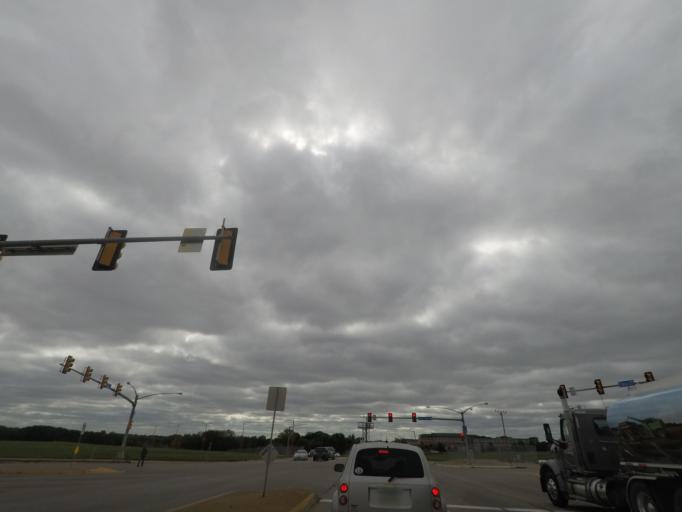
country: US
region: Iowa
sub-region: Warren County
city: Norwalk
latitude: 41.5267
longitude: -93.6459
